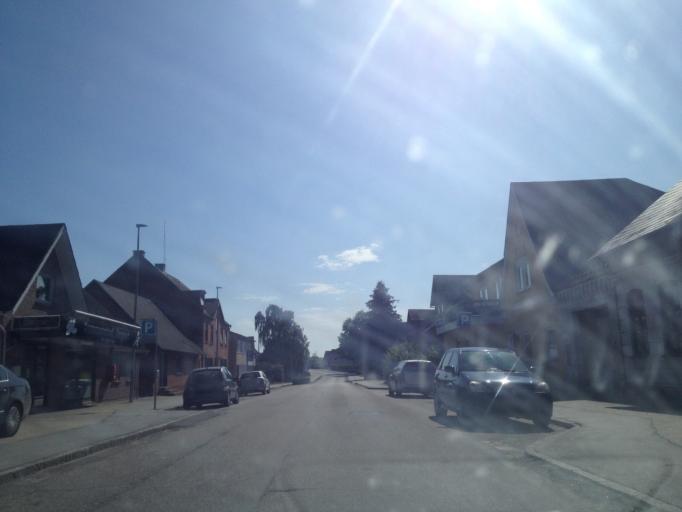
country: DK
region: South Denmark
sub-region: Haderslev Kommune
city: Vojens
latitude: 55.3130
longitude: 9.2859
